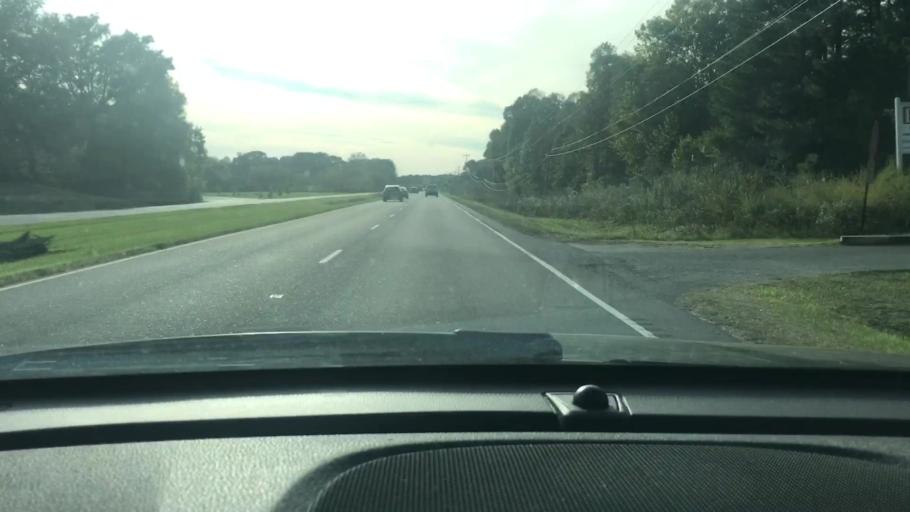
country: US
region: Tennessee
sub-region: Williamson County
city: Fairview
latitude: 35.9857
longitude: -87.1099
